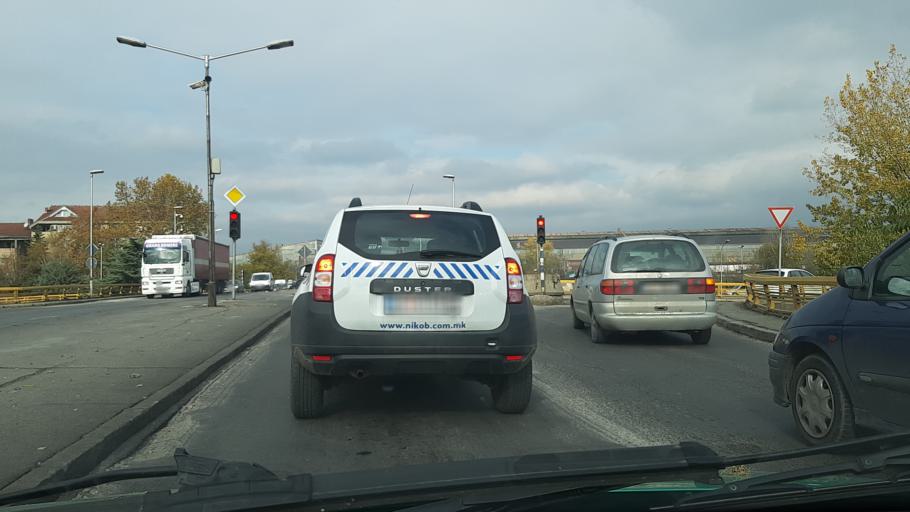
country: MK
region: Cair
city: Cair
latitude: 42.0021
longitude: 21.4709
